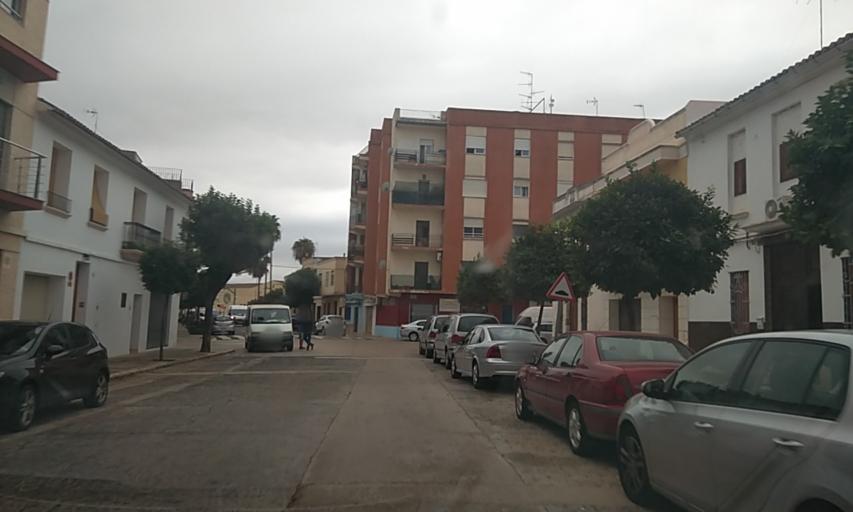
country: ES
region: Valencia
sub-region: Provincia de Valencia
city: L'Alcudia
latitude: 39.1930
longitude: -0.5093
